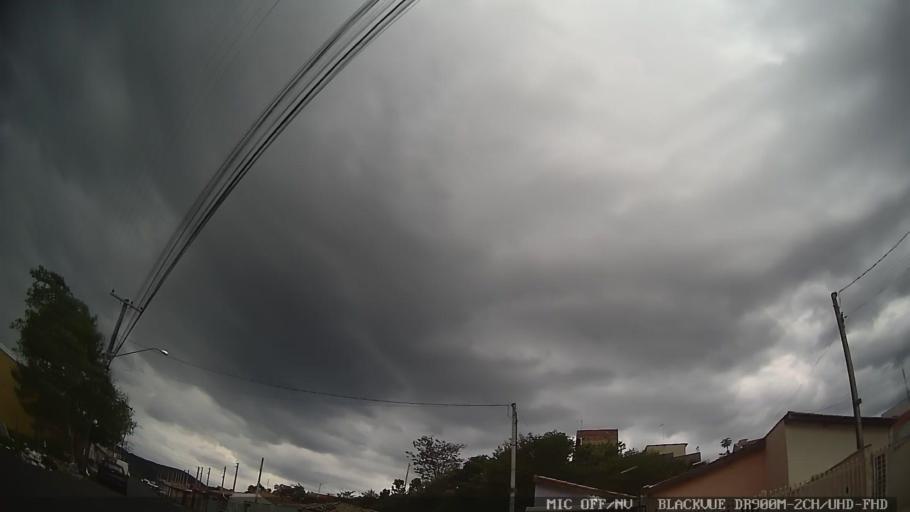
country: BR
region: Sao Paulo
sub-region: Amparo
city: Amparo
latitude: -22.7107
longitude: -46.8072
